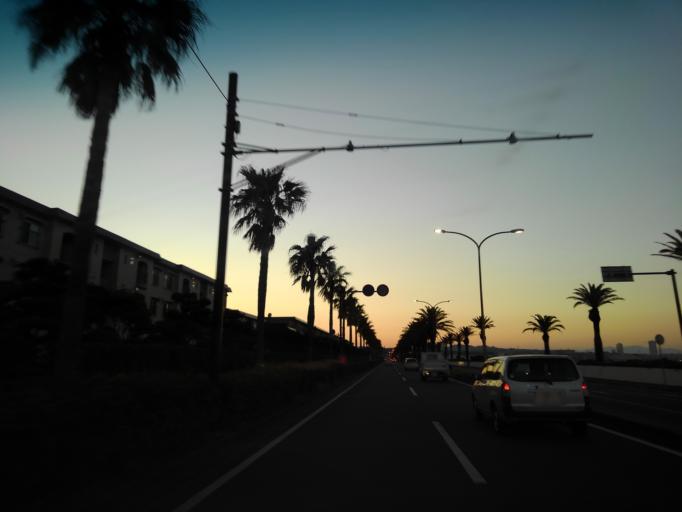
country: JP
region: Kanagawa
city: Yokosuka
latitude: 35.2634
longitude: 139.7117
